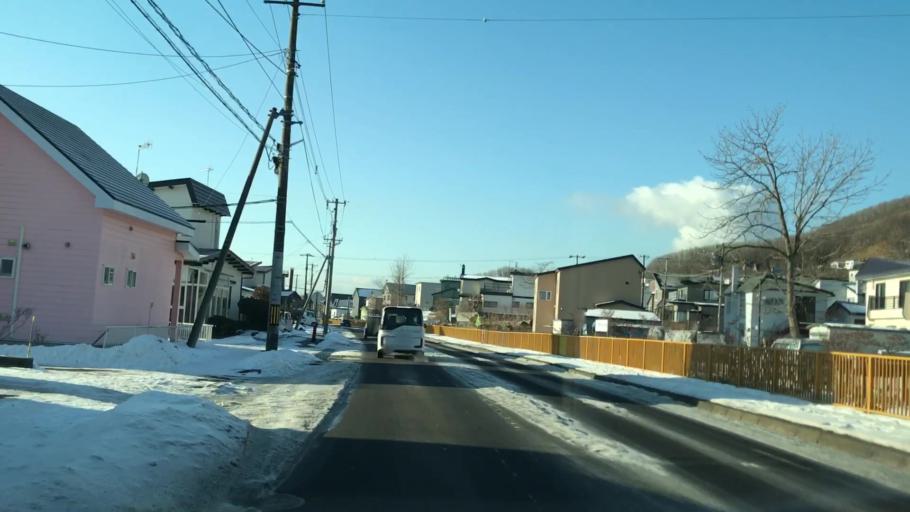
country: JP
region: Hokkaido
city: Muroran
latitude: 42.3703
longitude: 141.0520
